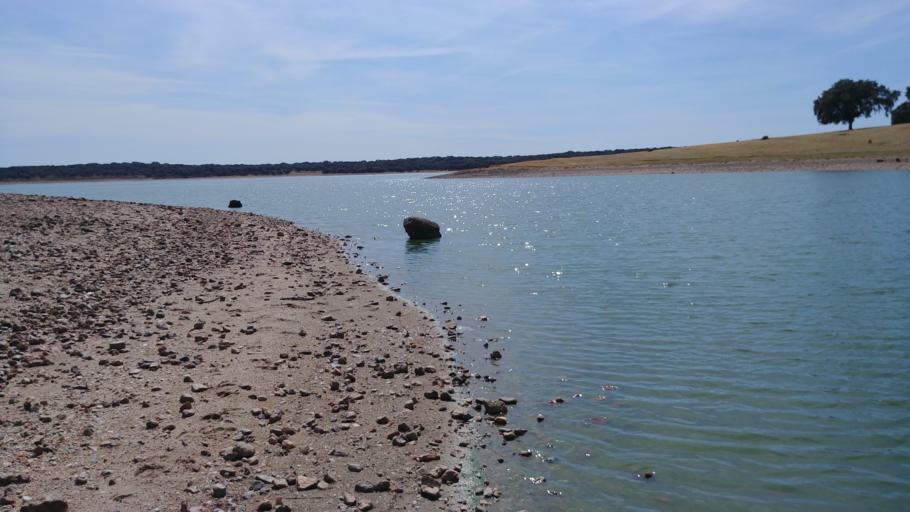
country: ES
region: Castille-La Mancha
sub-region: Province of Toledo
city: Navalcan
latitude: 40.0502
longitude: -5.1271
